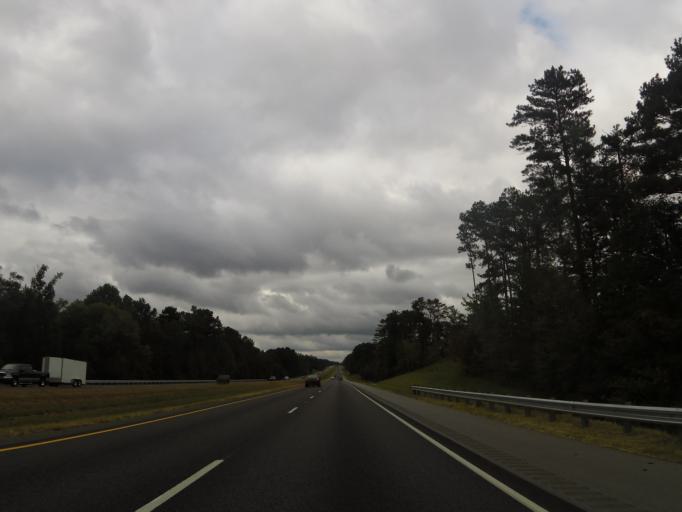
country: US
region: Alabama
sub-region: Conecuh County
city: Evergreen
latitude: 31.4765
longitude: -86.9494
